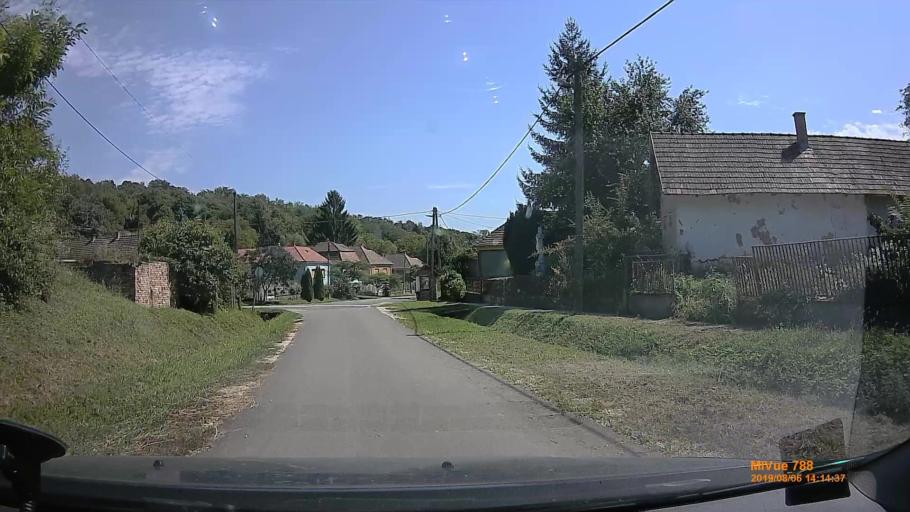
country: HU
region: Zala
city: Zalakomar
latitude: 46.5632
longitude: 17.0768
